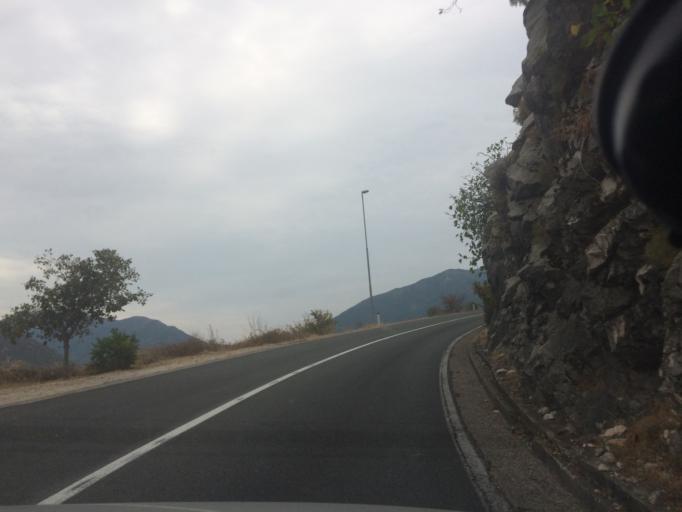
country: ME
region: Kotor
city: Risan
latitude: 42.5149
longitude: 18.6828
